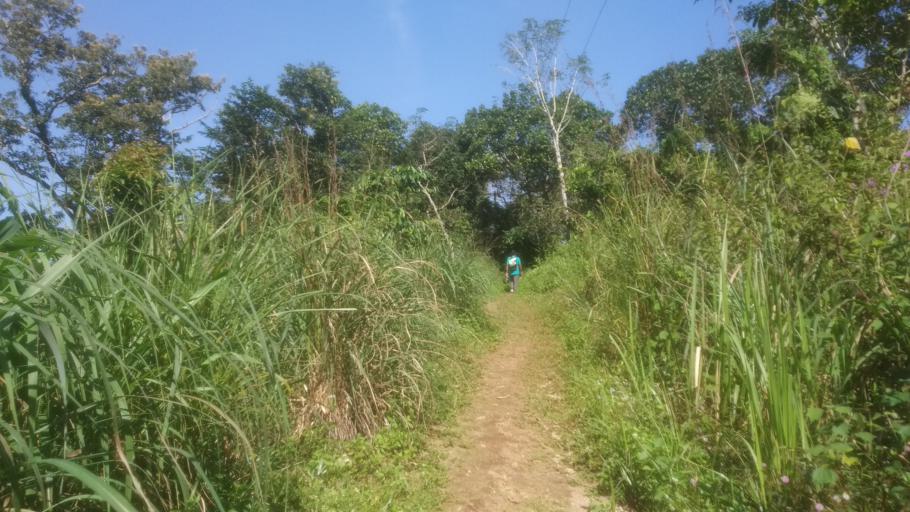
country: IN
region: Kerala
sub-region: Idukki
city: Idukki
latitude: 9.9800
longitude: 76.8328
